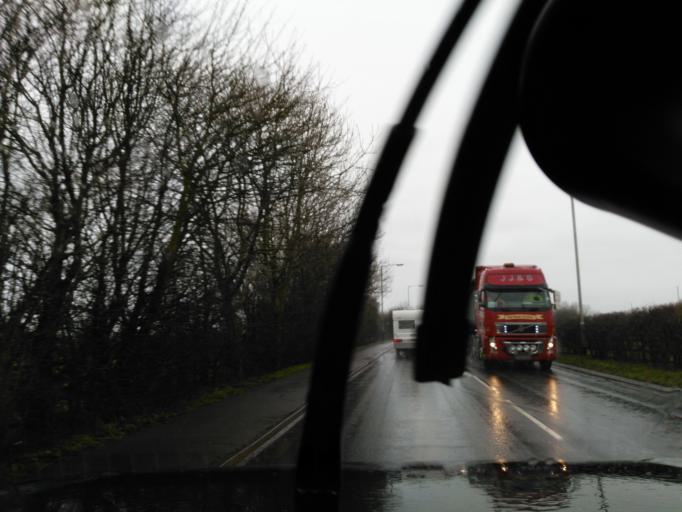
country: GB
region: England
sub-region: Somerset
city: Shepton Mallet
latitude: 51.1785
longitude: -2.5337
